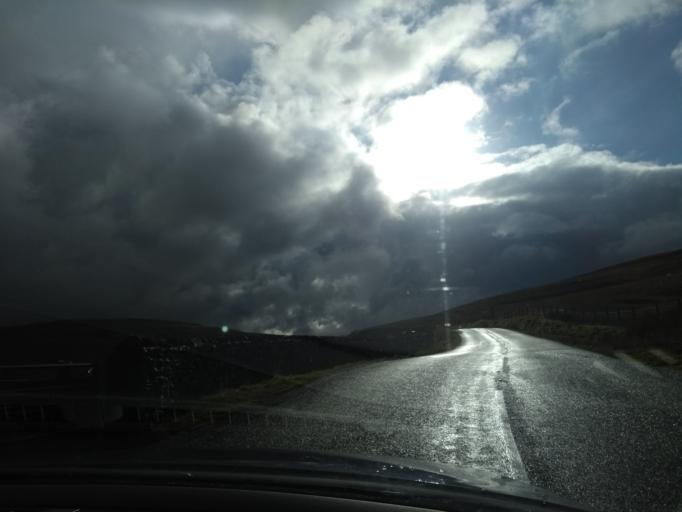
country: GB
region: England
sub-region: Cumbria
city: Kirkby Stephen
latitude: 54.3692
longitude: -2.1871
